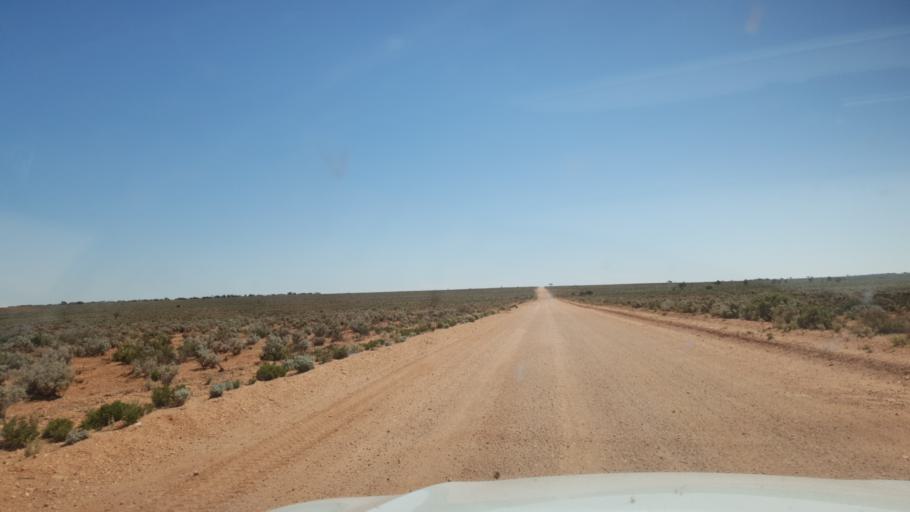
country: AU
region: South Australia
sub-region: Whyalla
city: Whyalla
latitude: -32.6458
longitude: 136.9528
